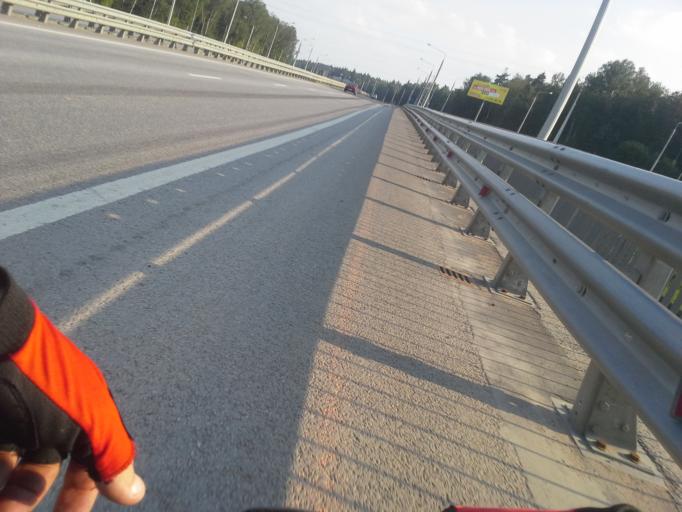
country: RU
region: Moskovskaya
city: Yershovo
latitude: 55.8236
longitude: 36.9181
